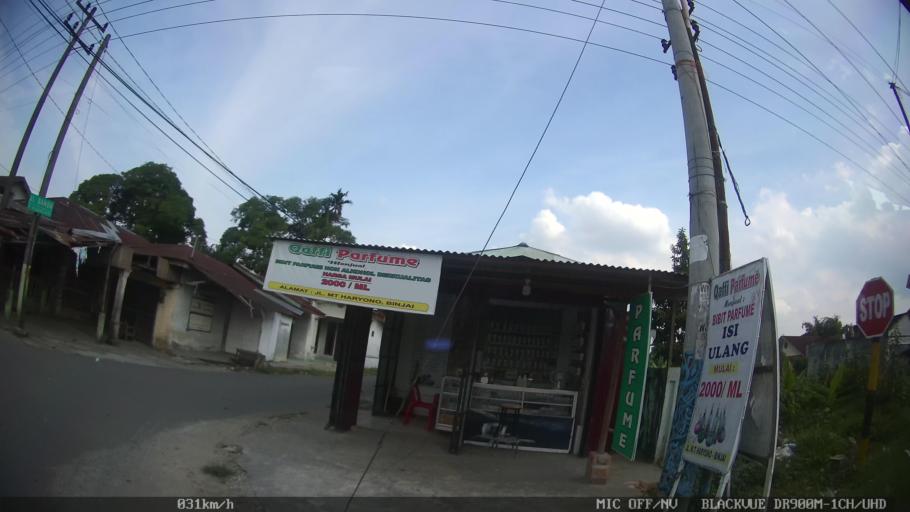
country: ID
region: North Sumatra
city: Binjai
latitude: 3.6366
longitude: 98.4912
